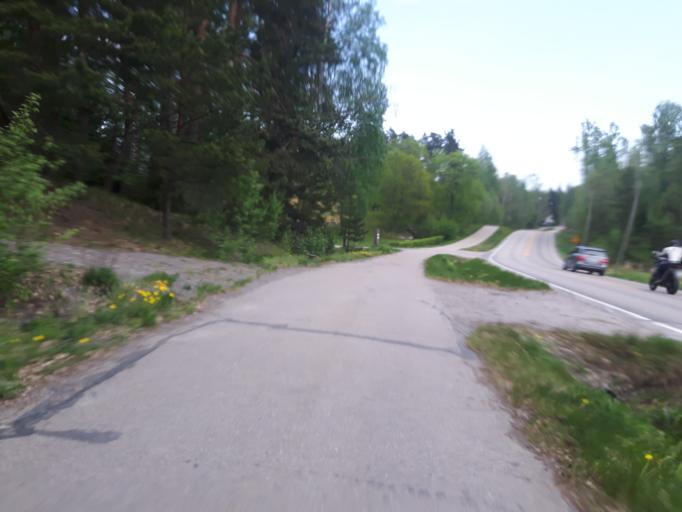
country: FI
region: Uusimaa
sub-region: Porvoo
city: Porvoo
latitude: 60.3951
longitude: 25.7365
